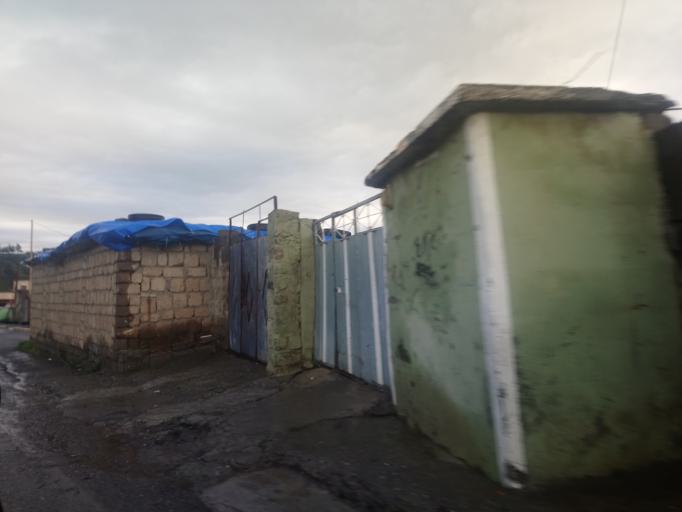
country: IQ
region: As Sulaymaniyah
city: Qeladize
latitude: 36.1855
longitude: 45.1163
